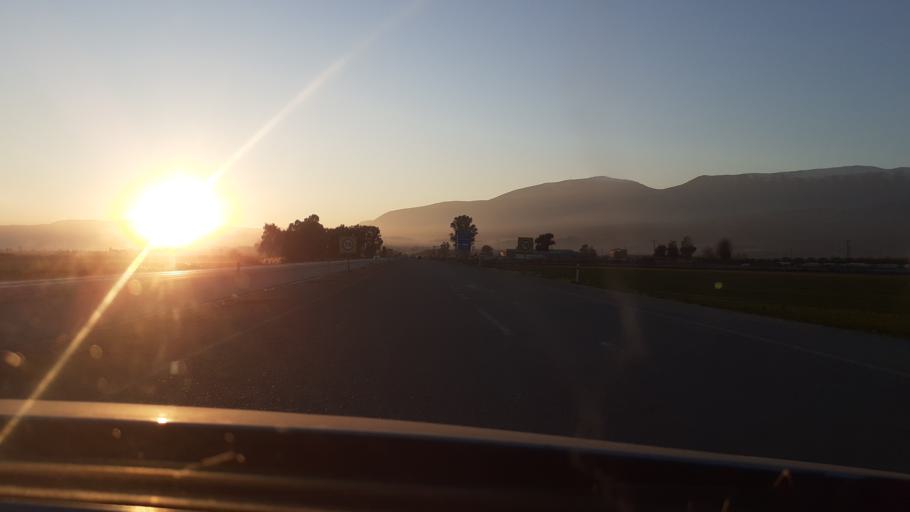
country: TR
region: Hatay
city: Kirikhan
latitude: 36.5057
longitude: 36.4194
